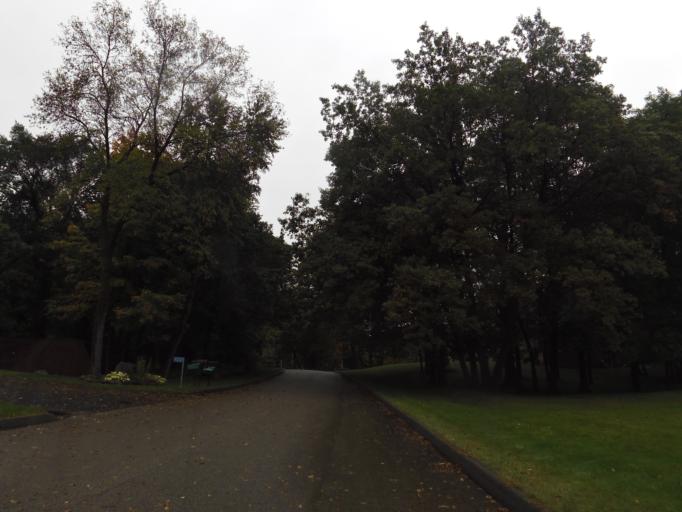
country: US
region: Minnesota
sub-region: Scott County
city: Prior Lake
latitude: 44.6824
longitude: -93.4357
